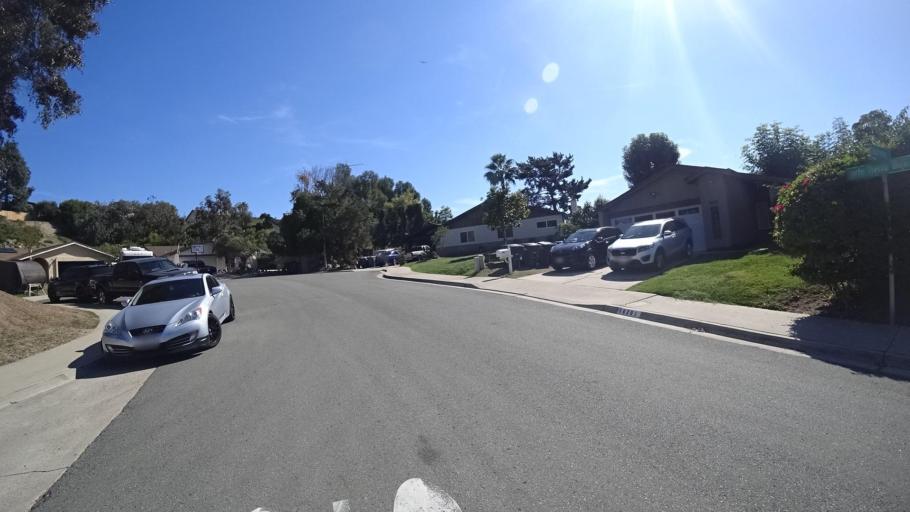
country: US
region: California
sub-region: San Diego County
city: Casa de Oro-Mount Helix
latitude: 32.7520
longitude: -116.9745
